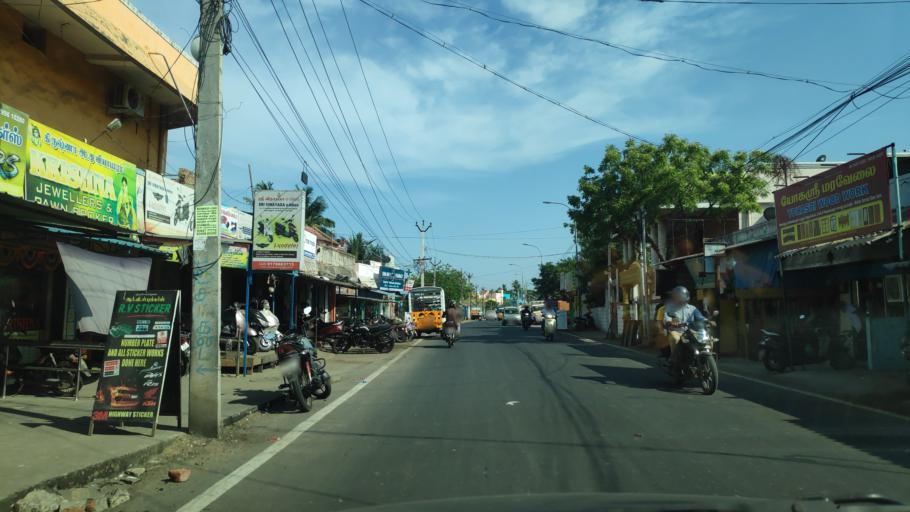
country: IN
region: Tamil Nadu
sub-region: Thiruvallur
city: Ambattur
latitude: 13.1215
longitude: 80.1678
